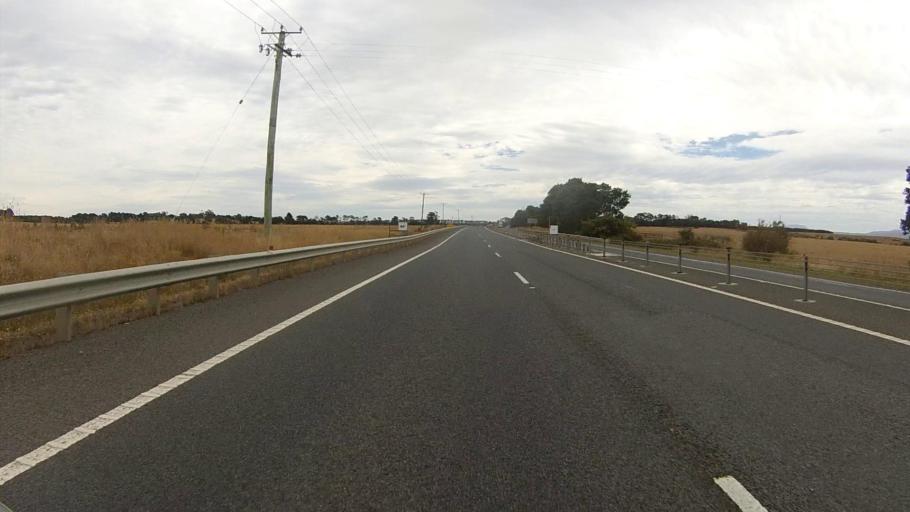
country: AU
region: Tasmania
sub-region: Northern Midlands
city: Evandale
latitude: -41.6375
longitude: 147.2316
